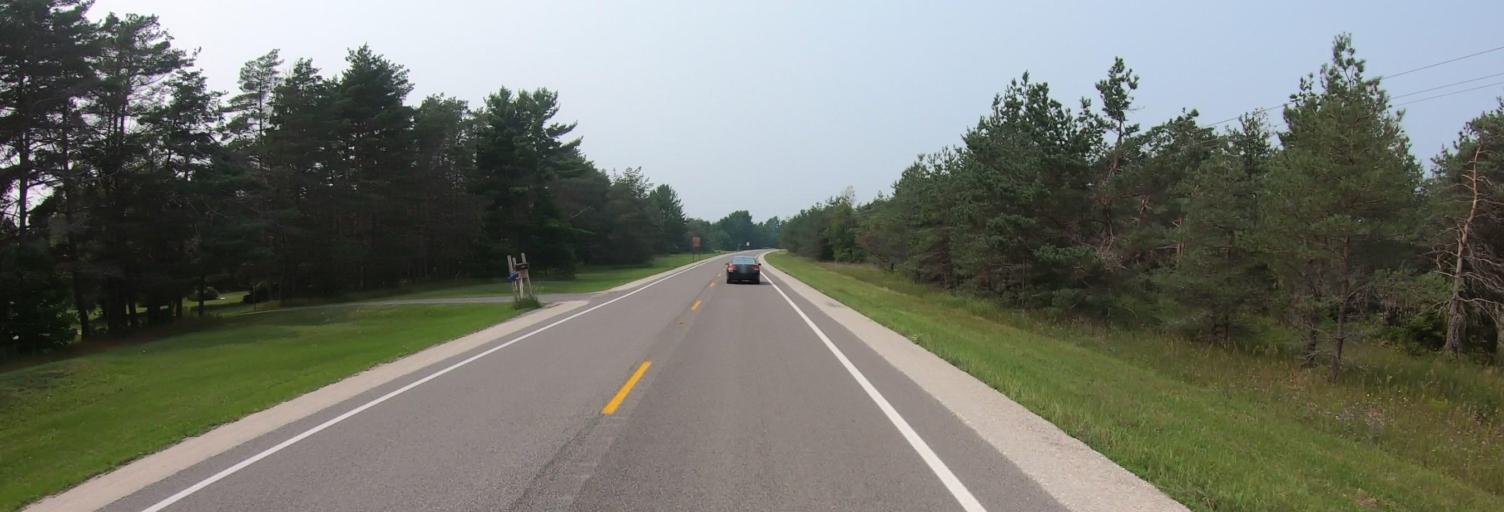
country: US
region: Michigan
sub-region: Chippewa County
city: Sault Ste. Marie
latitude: 46.0270
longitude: -84.0787
